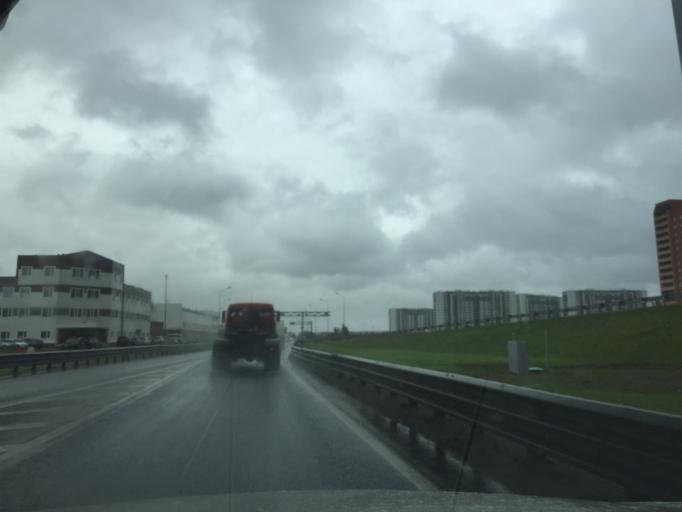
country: RU
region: St.-Petersburg
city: Sosnovaya Polyana
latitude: 59.7979
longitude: 30.1596
